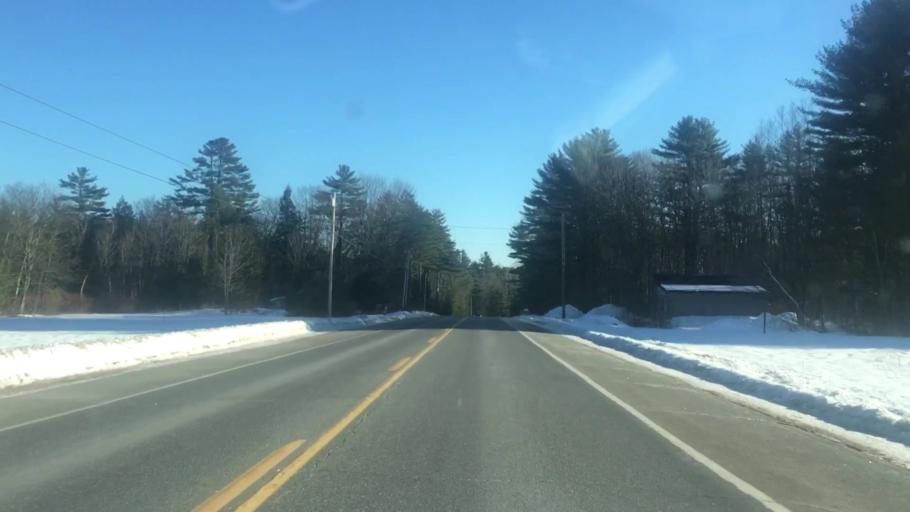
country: US
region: Maine
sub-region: Somerset County
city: Norridgewock
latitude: 44.7469
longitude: -69.8335
